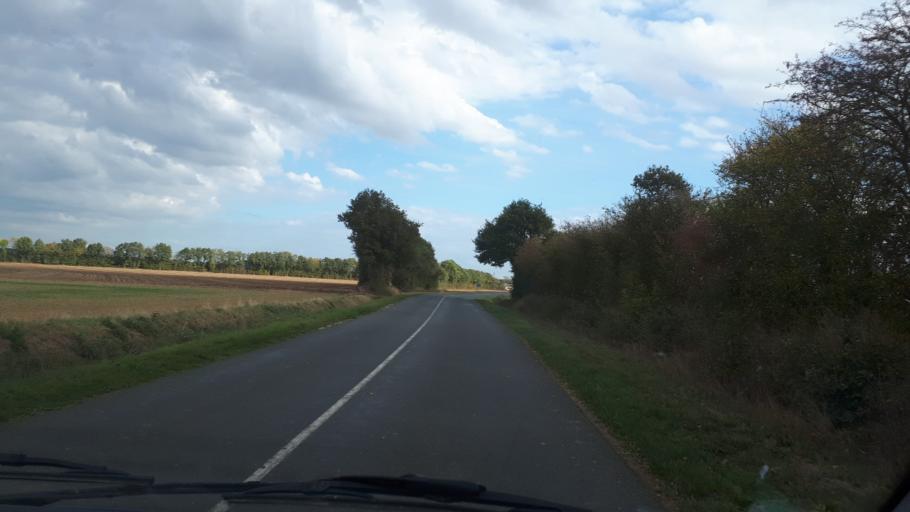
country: FR
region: Centre
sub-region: Departement d'Eure-et-Loir
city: La Bazoche-Gouet
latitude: 48.0705
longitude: 0.9553
